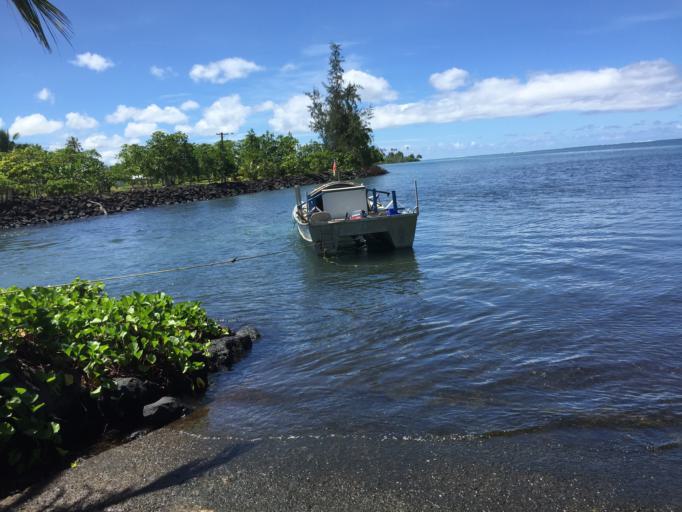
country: WS
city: Matavai
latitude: -14.0288
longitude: -171.6946
